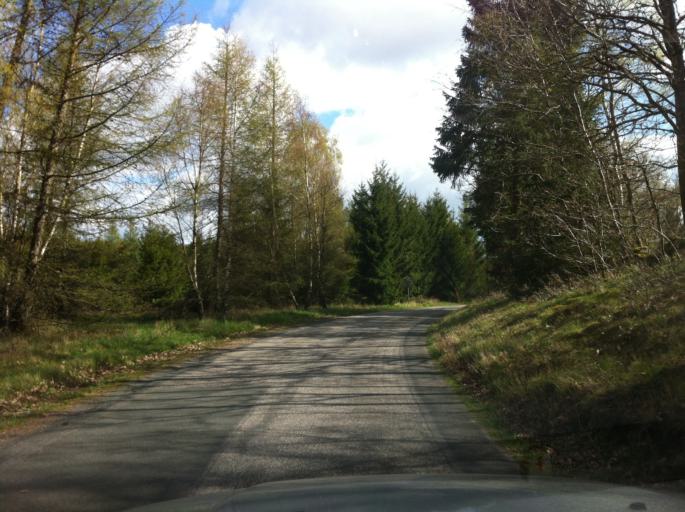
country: SE
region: Skane
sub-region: Hoors Kommun
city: Satofta
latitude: 55.9120
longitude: 13.6115
